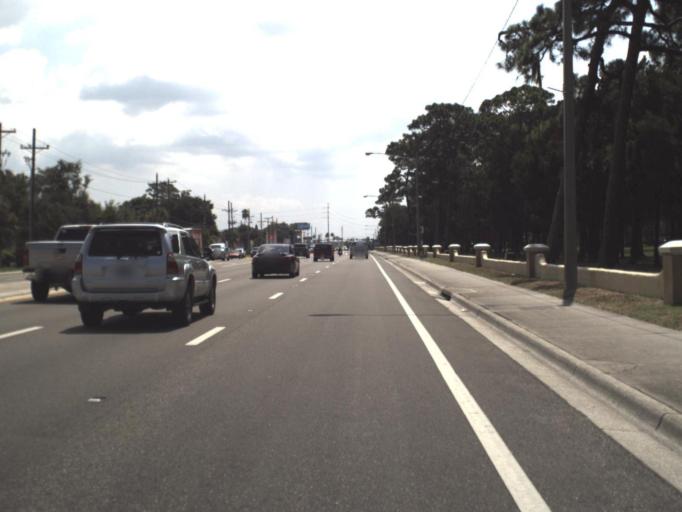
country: US
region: Florida
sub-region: Pinellas County
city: Bay Pines
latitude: 27.8138
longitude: -82.7768
